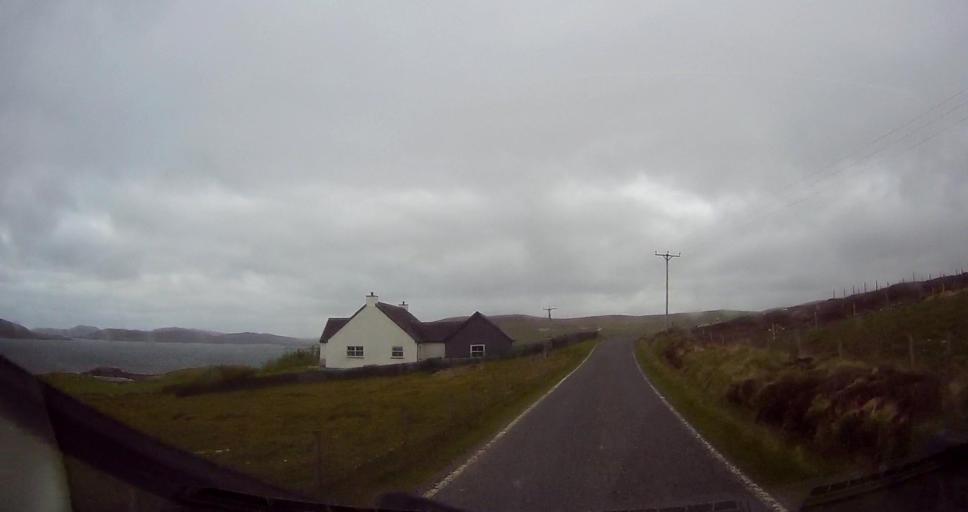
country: GB
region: Scotland
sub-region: Shetland Islands
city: Lerwick
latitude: 60.2960
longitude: -1.3640
